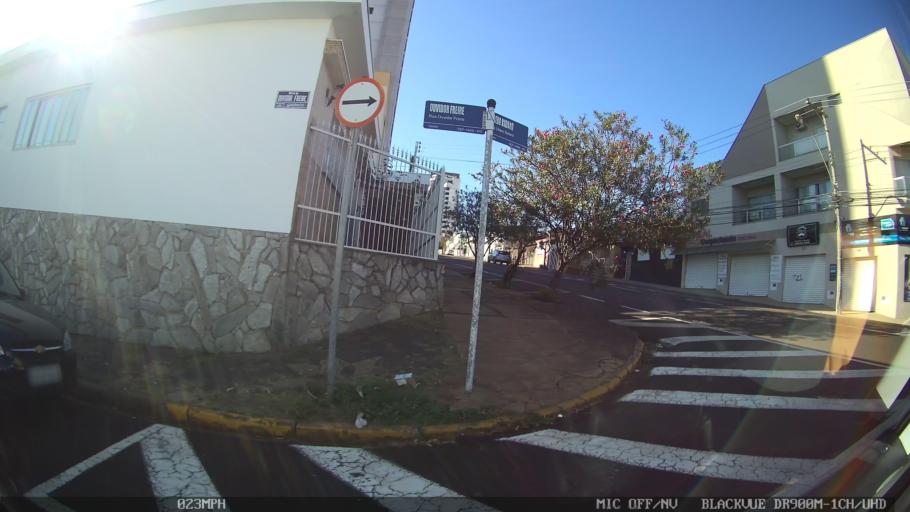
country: BR
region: Sao Paulo
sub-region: Franca
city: Franca
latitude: -20.5318
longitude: -47.4014
